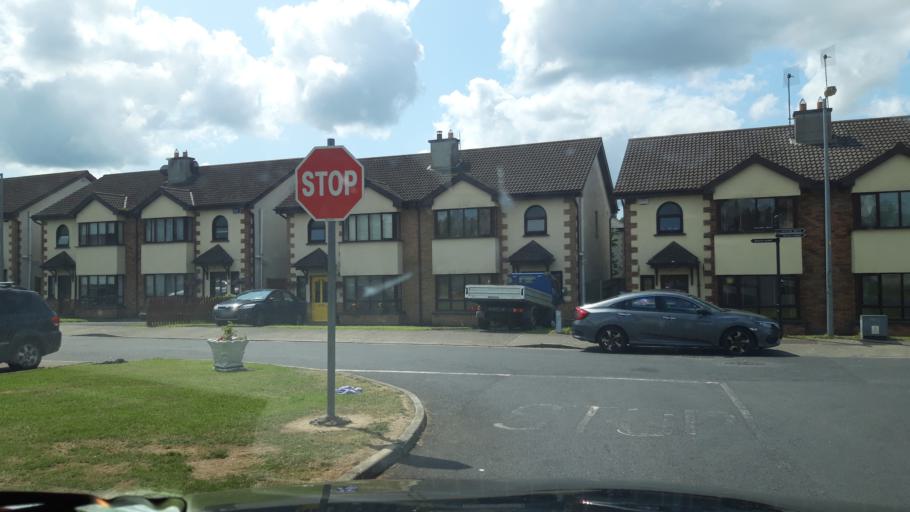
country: IE
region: Munster
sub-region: Waterford
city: Waterford
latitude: 52.2670
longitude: -7.0914
